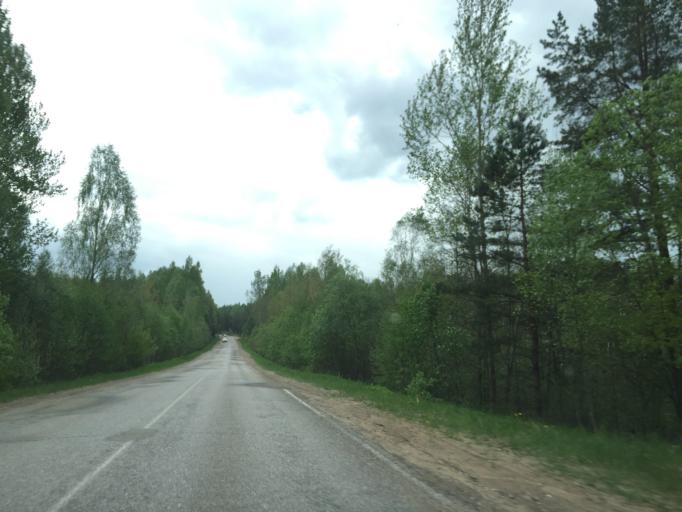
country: LV
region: Ogre
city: Ogre
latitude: 56.8406
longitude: 24.5759
